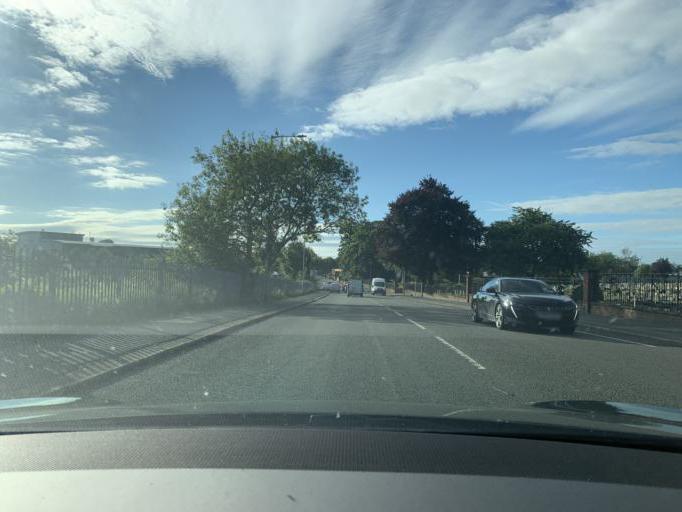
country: GB
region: England
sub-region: Staffordshire
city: Stafford
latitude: 52.8167
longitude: -2.1269
